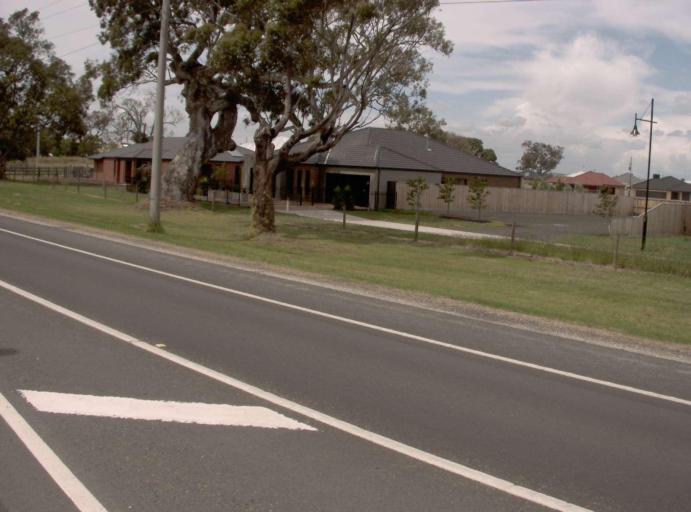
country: AU
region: Victoria
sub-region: Wellington
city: Sale
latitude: -38.0837
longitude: 147.0554
